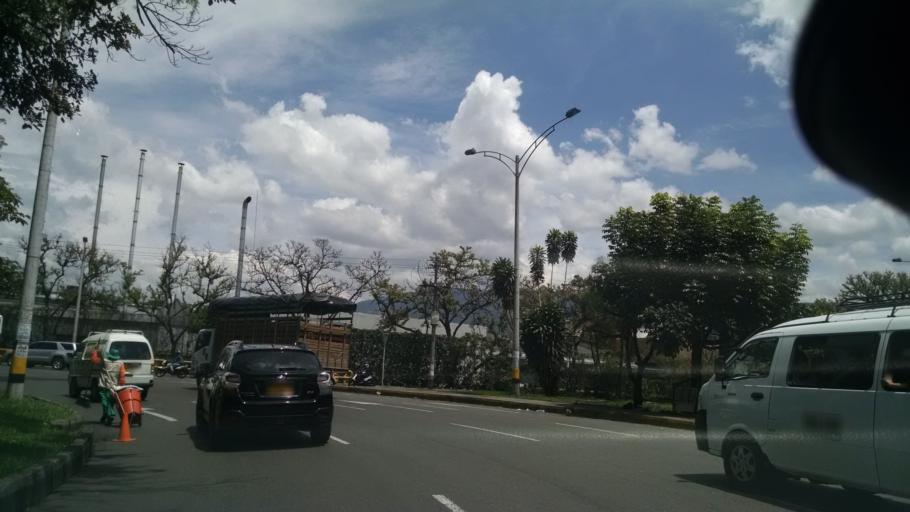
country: CO
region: Antioquia
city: Itagui
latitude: 6.2166
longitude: -75.5857
